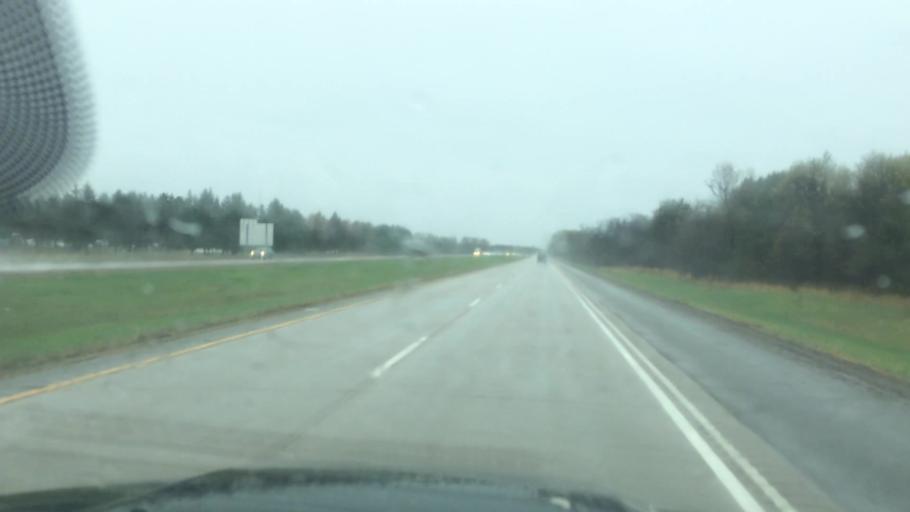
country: US
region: Wisconsin
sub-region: Marathon County
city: Mosinee
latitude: 44.6578
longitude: -89.6419
